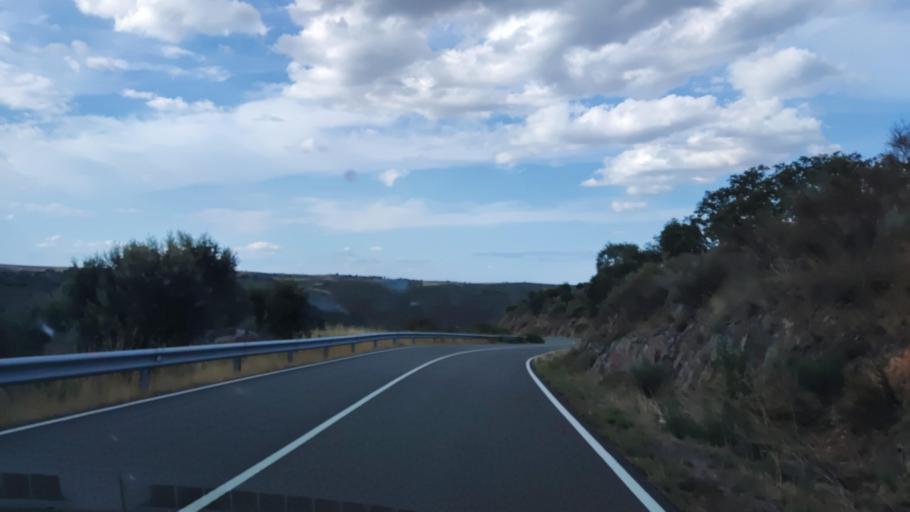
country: ES
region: Castille and Leon
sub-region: Provincia de Salamanca
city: Pastores
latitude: 40.4909
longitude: -6.4965
